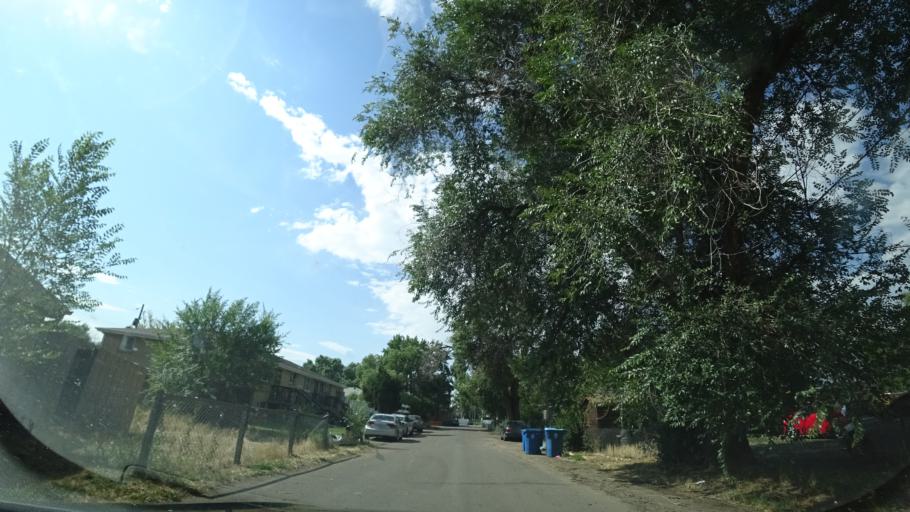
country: US
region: Colorado
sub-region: Jefferson County
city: Edgewater
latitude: 39.7231
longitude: -105.0564
